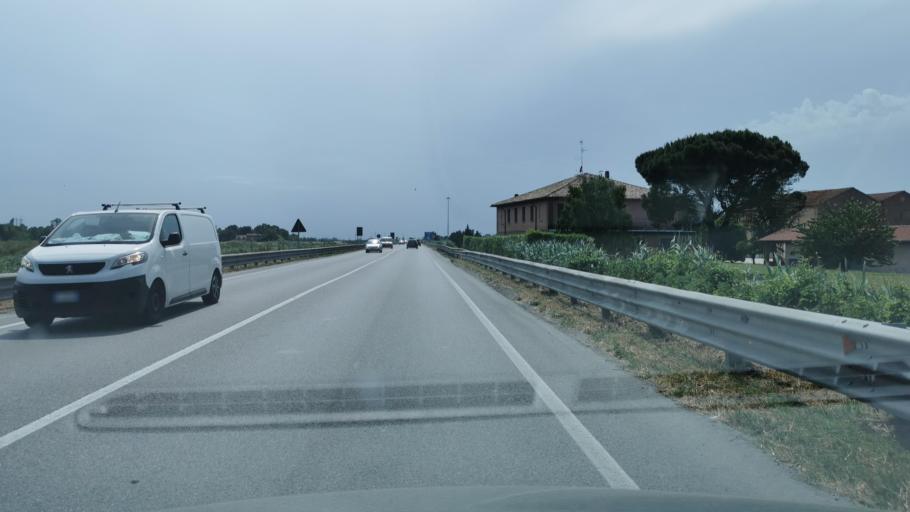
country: IT
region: Emilia-Romagna
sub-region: Provincia di Ravenna
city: Ravenna
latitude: 44.4517
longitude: 12.1974
